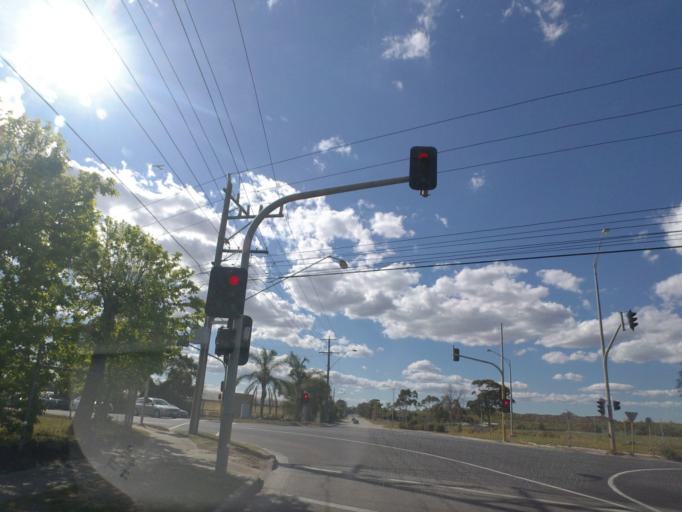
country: AU
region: Victoria
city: Heatherton
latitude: -37.9562
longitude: 145.1002
